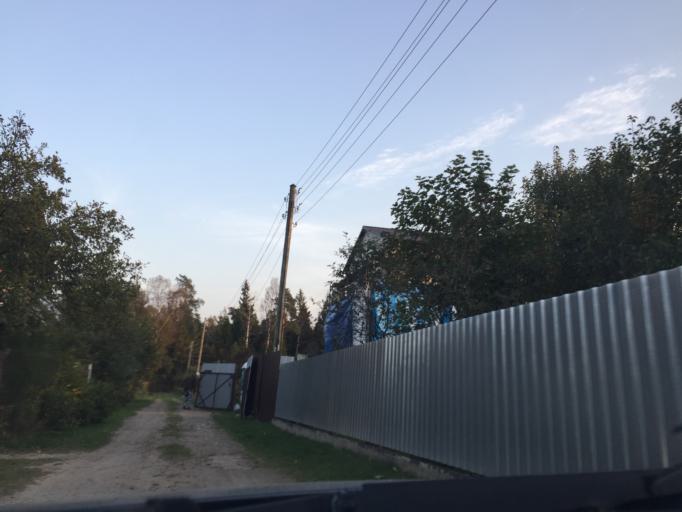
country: LV
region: Salaspils
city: Salaspils
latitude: 56.9187
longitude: 24.4337
